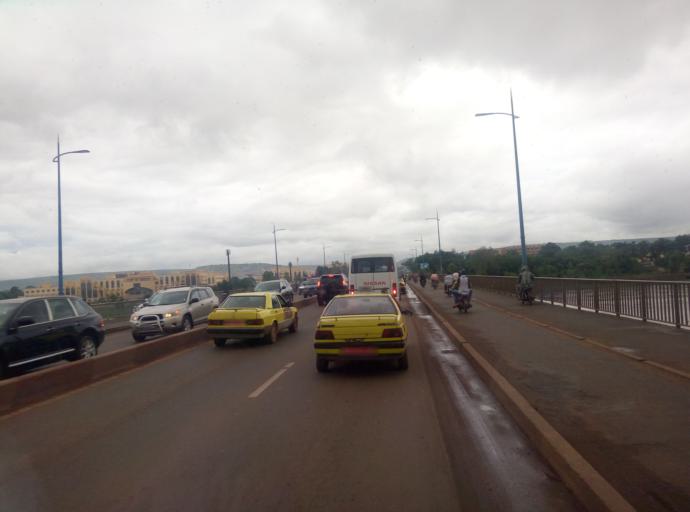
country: ML
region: Bamako
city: Bamako
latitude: 12.6252
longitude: -8.0058
